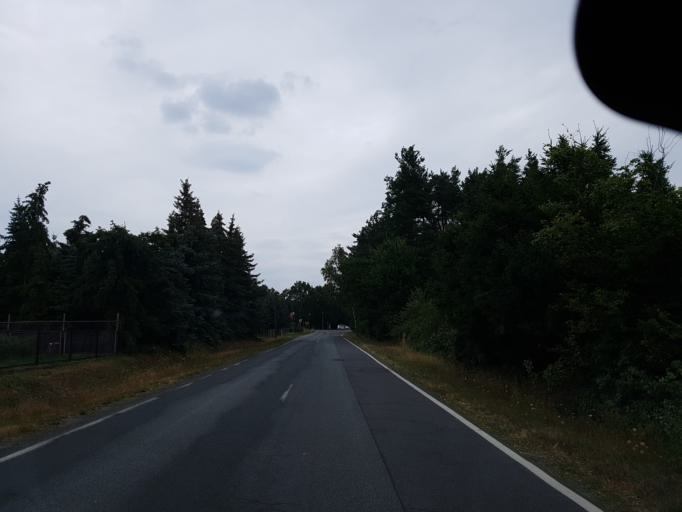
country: DE
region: Brandenburg
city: Sallgast
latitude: 51.6110
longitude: 13.8438
